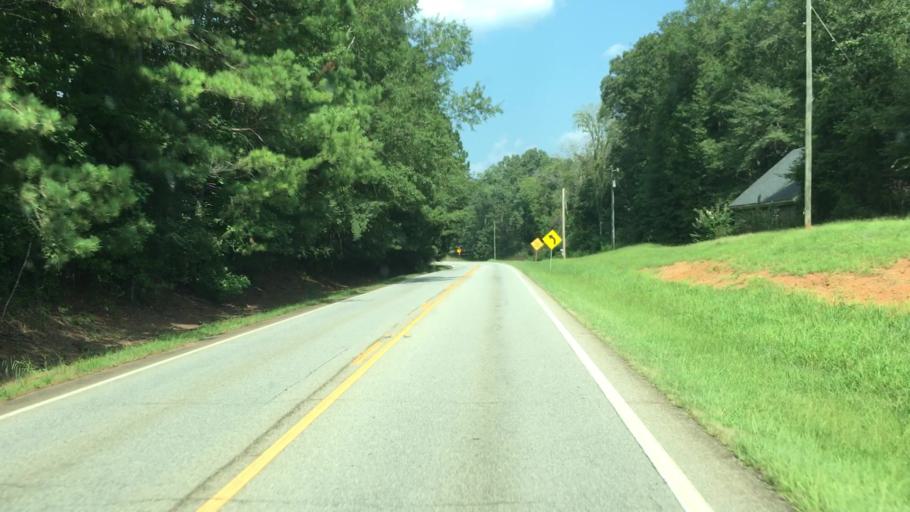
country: US
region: Georgia
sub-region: Butts County
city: Indian Springs
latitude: 33.1522
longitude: -83.8336
